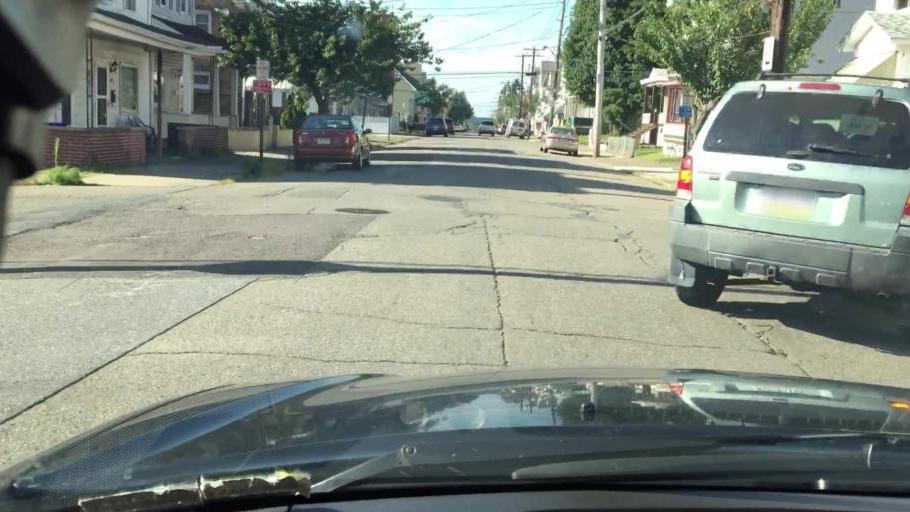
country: US
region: Pennsylvania
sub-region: Luzerne County
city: Hazleton
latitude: 40.9627
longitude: -75.9786
